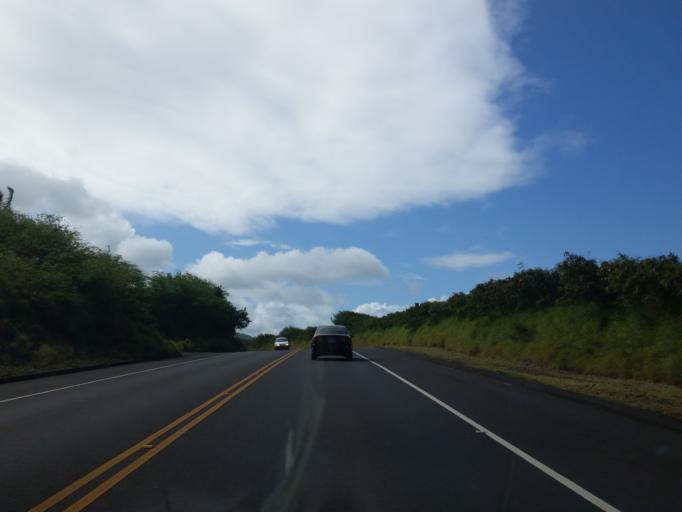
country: US
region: Hawaii
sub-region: Maui County
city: Waihee-Waiehu
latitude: 20.9160
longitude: -156.4951
